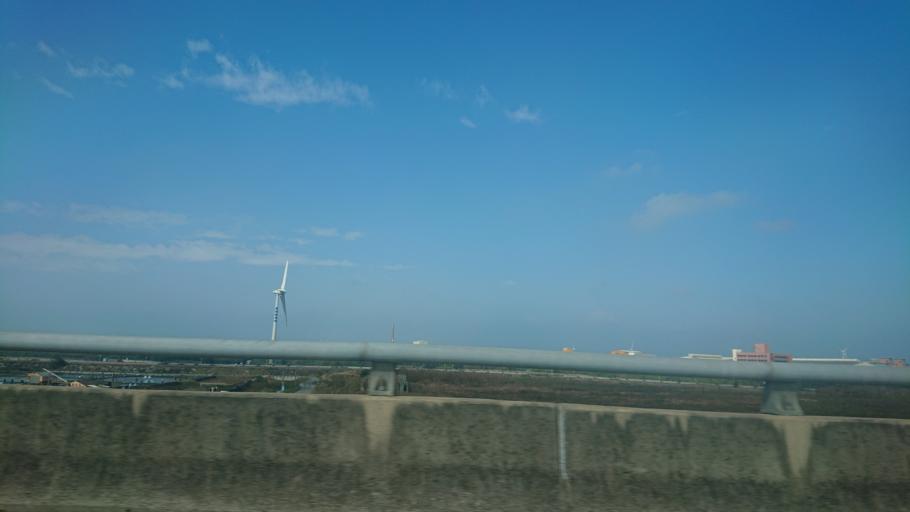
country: TW
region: Taiwan
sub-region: Changhua
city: Chang-hua
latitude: 24.0699
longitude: 120.4138
